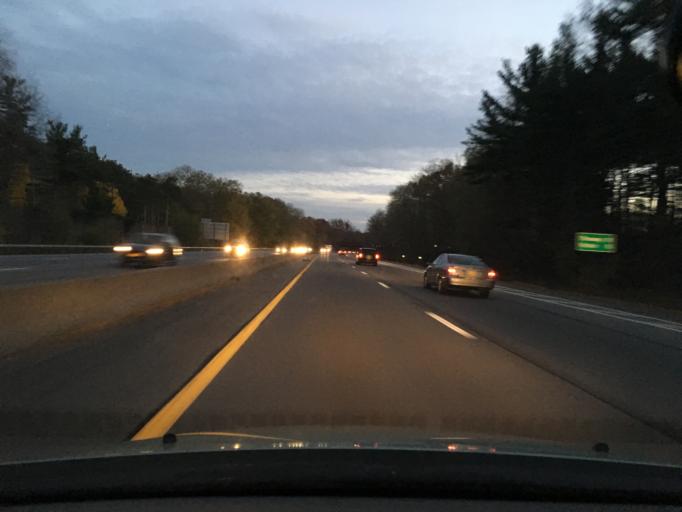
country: US
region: New York
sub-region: Monroe County
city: Pittsford
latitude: 43.1010
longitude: -77.5034
